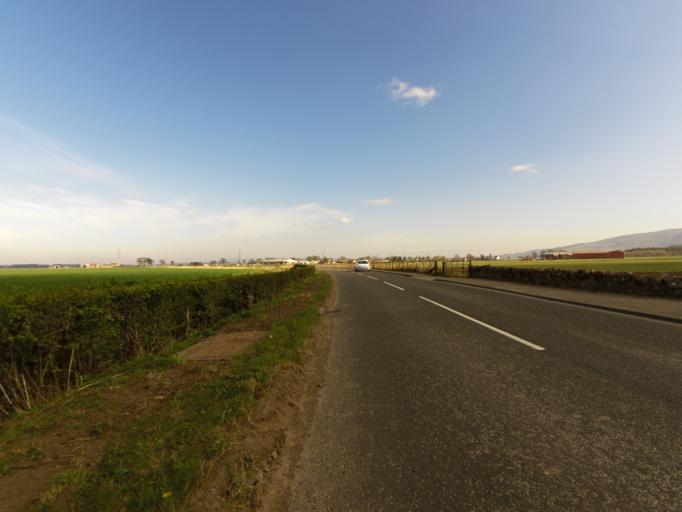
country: GB
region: Scotland
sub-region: Fife
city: Auchtermuchty
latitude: 56.2846
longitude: -3.2232
